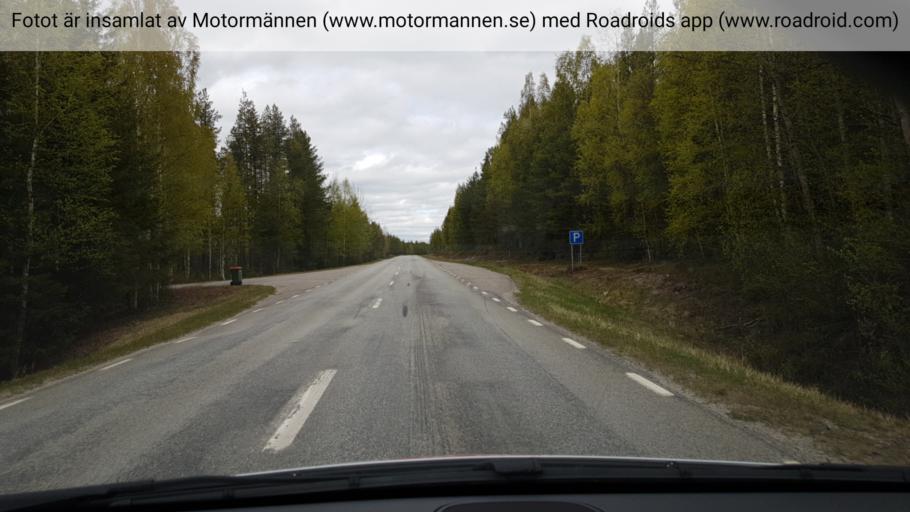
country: SE
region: Vaesterbotten
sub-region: Lycksele Kommun
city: Lycksele
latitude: 64.8371
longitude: 18.7730
